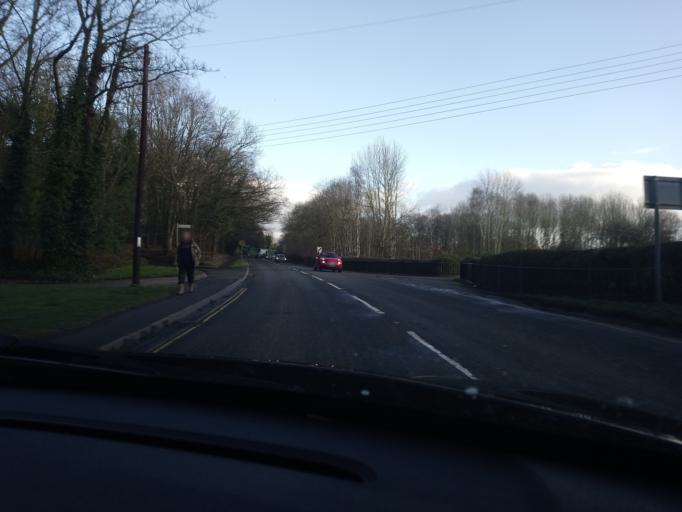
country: GB
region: England
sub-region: Shropshire
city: Ellesmere
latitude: 52.9022
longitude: -2.8798
